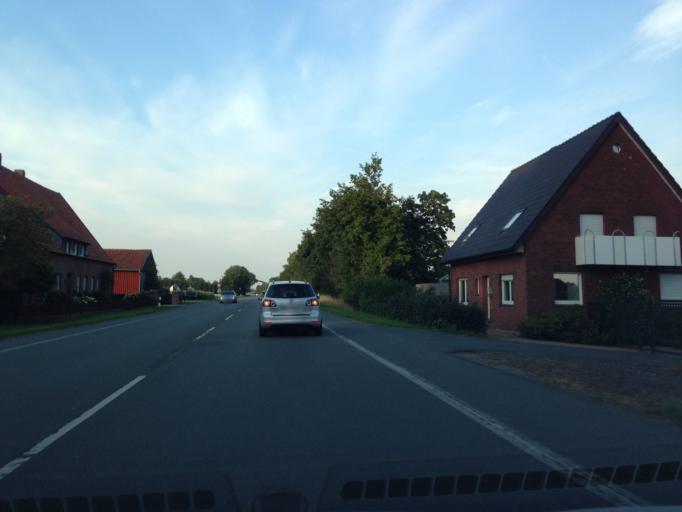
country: DE
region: North Rhine-Westphalia
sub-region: Regierungsbezirk Munster
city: Senden
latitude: 51.8716
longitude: 7.5579
